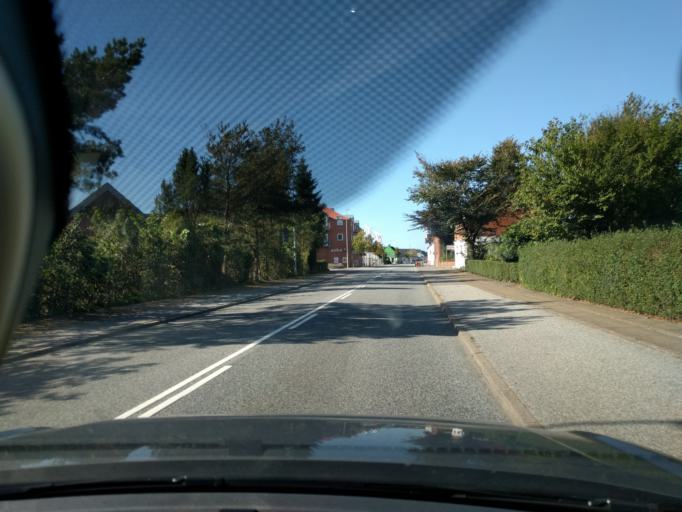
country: DK
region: North Denmark
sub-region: Vesthimmerland Kommune
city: Alestrup
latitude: 56.7061
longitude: 9.6329
